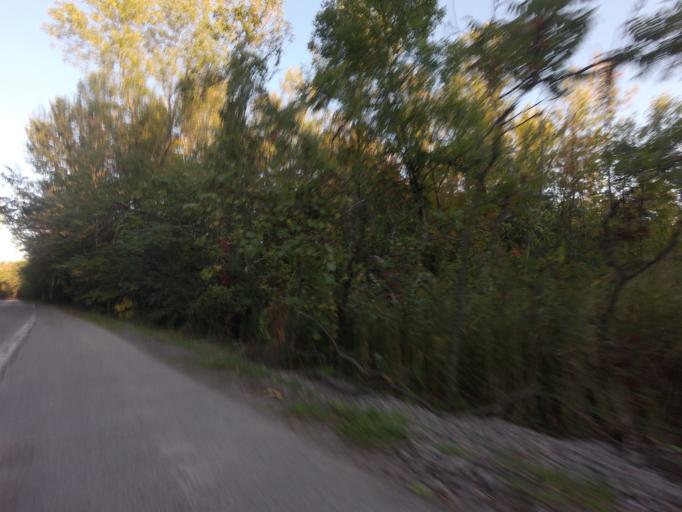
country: CA
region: Quebec
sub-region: Monteregie
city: Hudson
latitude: 45.4535
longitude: -74.1291
